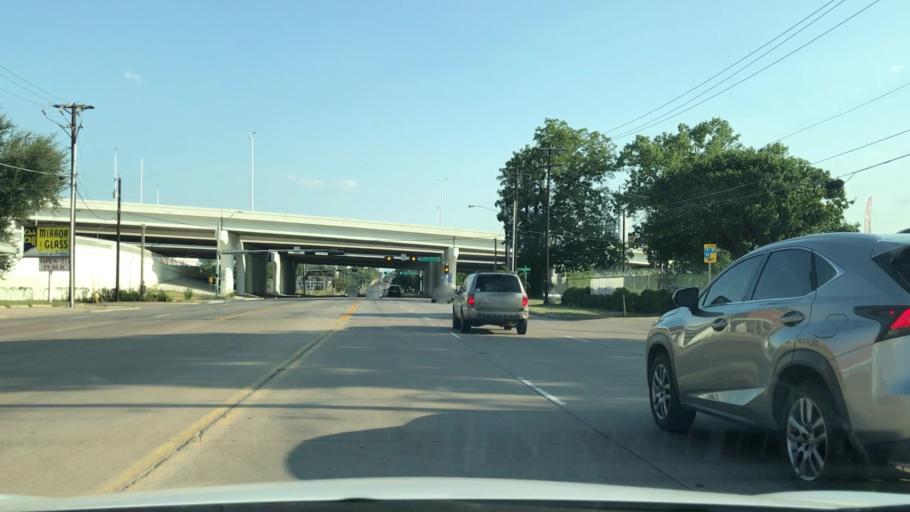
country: US
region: Texas
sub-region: Dallas County
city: Dallas
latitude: 32.7707
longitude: -96.8229
